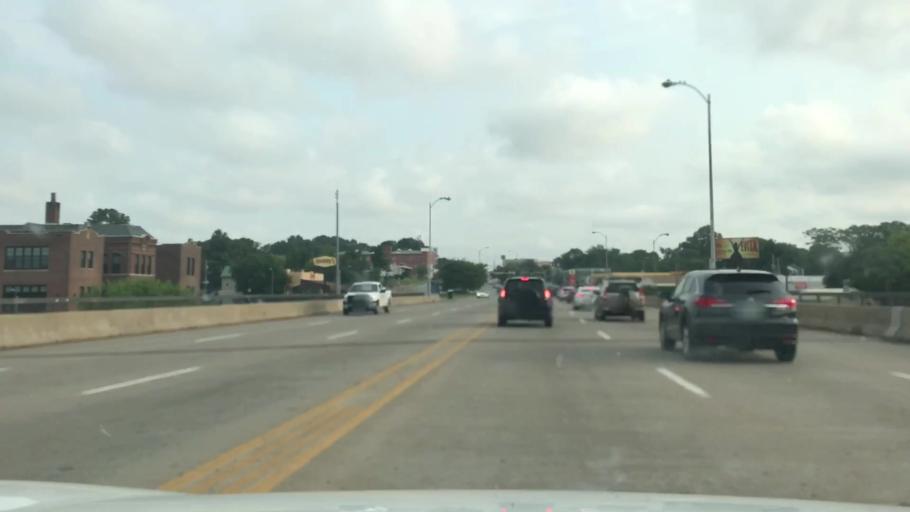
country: US
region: Missouri
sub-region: Saint Louis County
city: Richmond Heights
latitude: 38.6217
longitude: -90.2882
